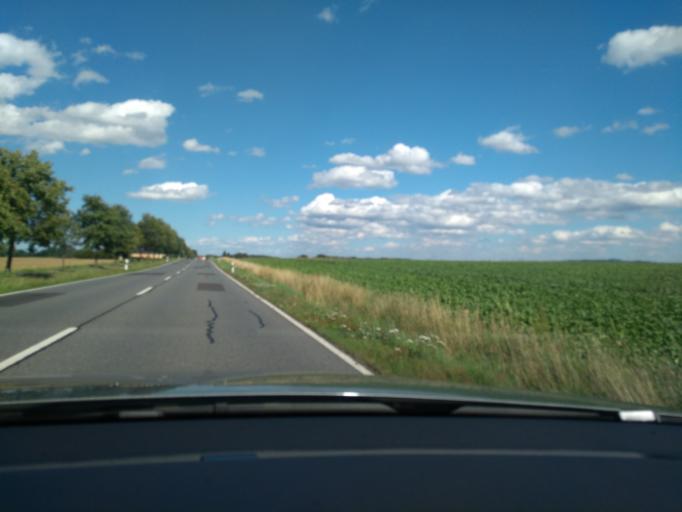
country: DE
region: Saxony
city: Demitz-Thumitz
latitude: 51.1574
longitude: 14.2575
